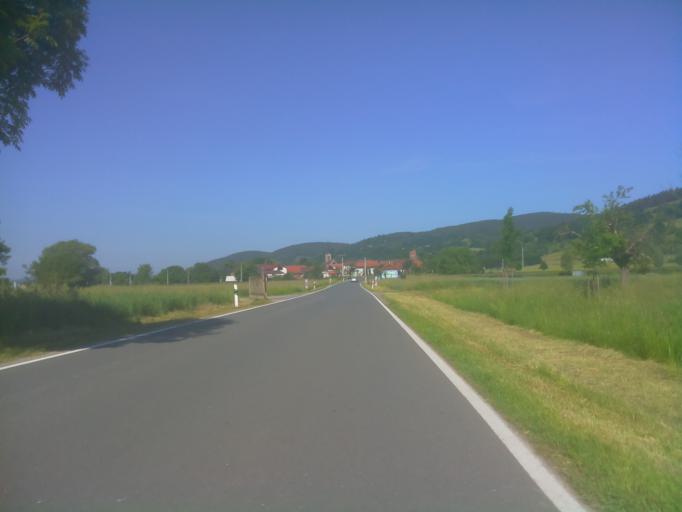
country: DE
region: Thuringia
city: Reinstadt
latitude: 50.7356
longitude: 11.4417
